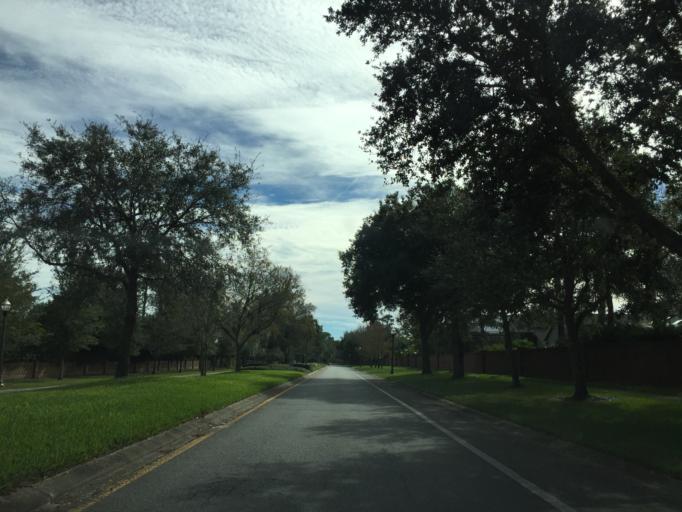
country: US
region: Florida
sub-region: Seminole County
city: Oviedo
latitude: 28.6725
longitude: -81.2360
